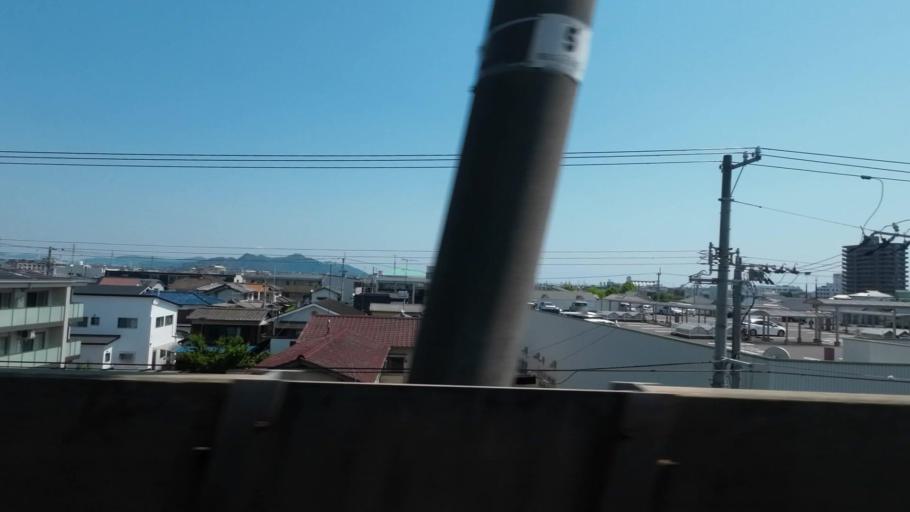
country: JP
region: Ehime
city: Hojo
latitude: 34.0695
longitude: 132.9888
